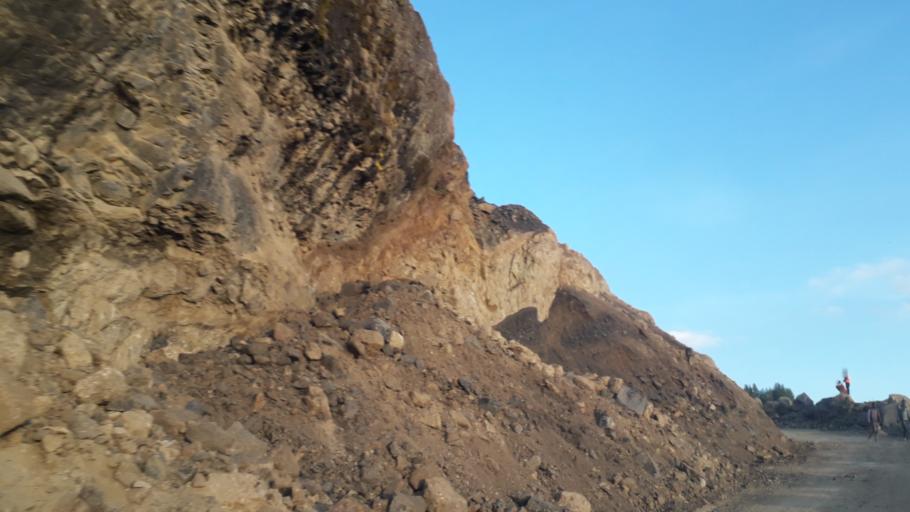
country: ET
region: Amhara
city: Lalibela
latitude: 11.5533
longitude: 39.2206
